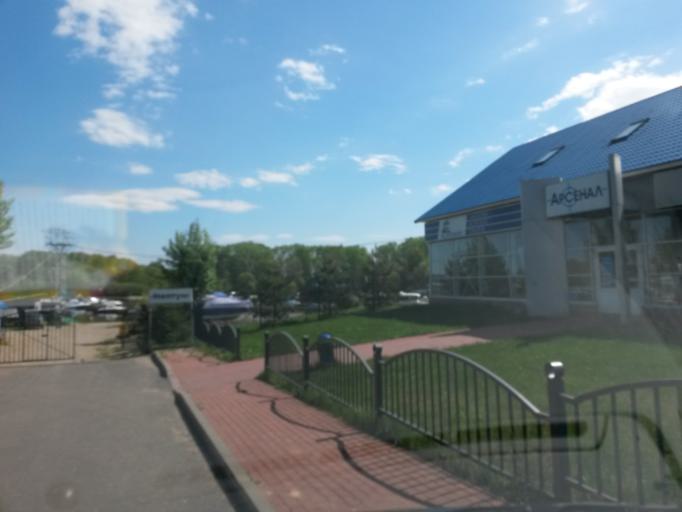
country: RU
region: Jaroslavl
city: Yaroslavl
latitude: 57.6178
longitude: 39.8728
